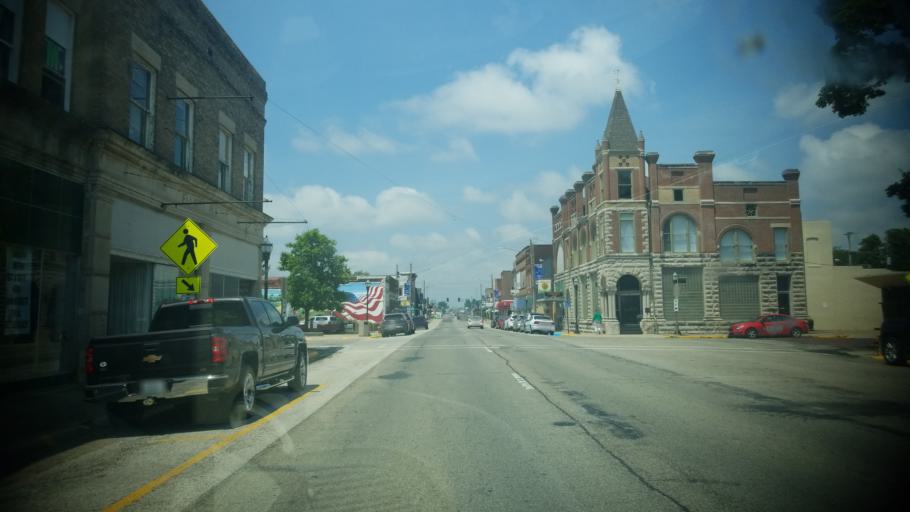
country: US
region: Illinois
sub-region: Wayne County
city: Fairfield
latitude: 38.3796
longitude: -88.3574
